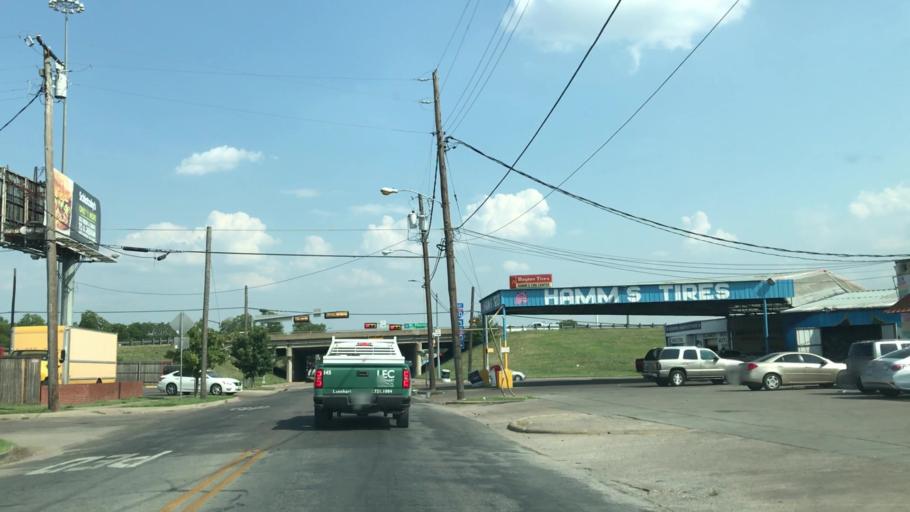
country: US
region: Texas
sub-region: Dallas County
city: Dallas
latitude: 32.7897
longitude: -96.7653
